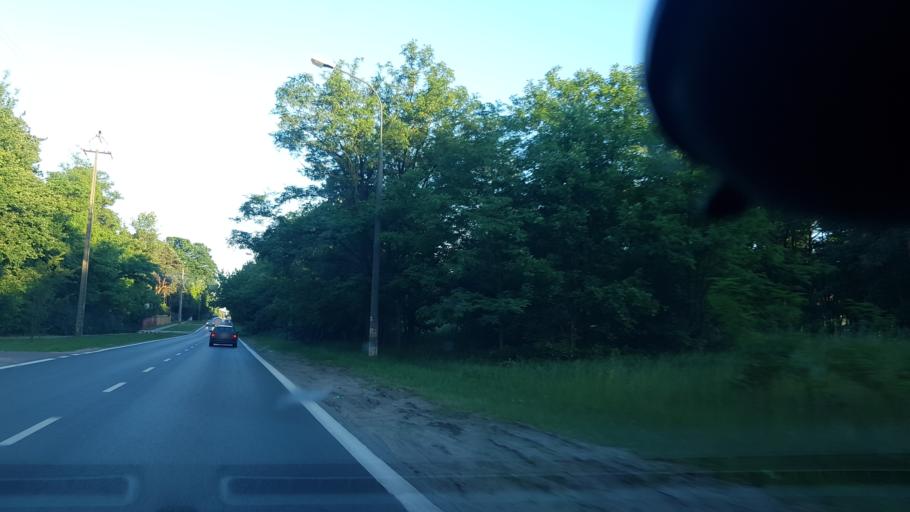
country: PL
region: Masovian Voivodeship
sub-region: Warszawa
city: Wawer
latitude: 52.1802
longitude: 21.1933
